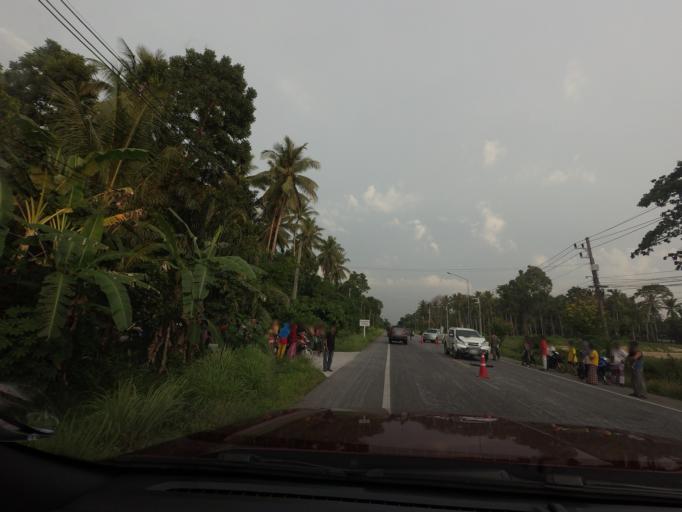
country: TH
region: Pattani
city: Mae Lan
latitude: 6.5974
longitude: 101.1946
